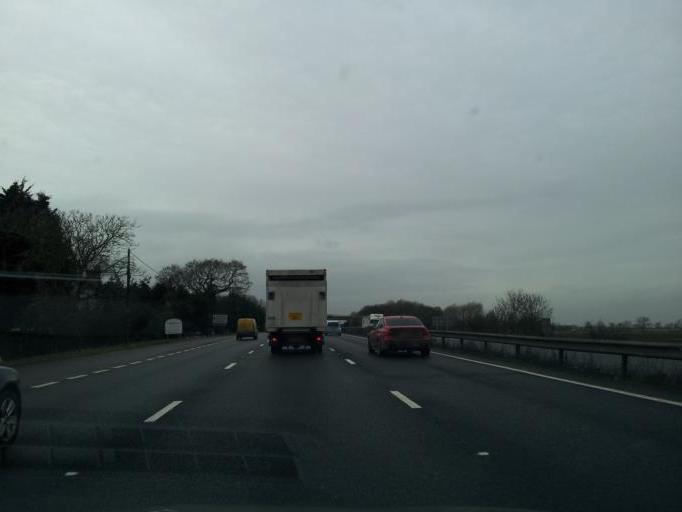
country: GB
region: England
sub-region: Cambridgeshire
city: Girton
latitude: 52.2456
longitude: 0.0479
